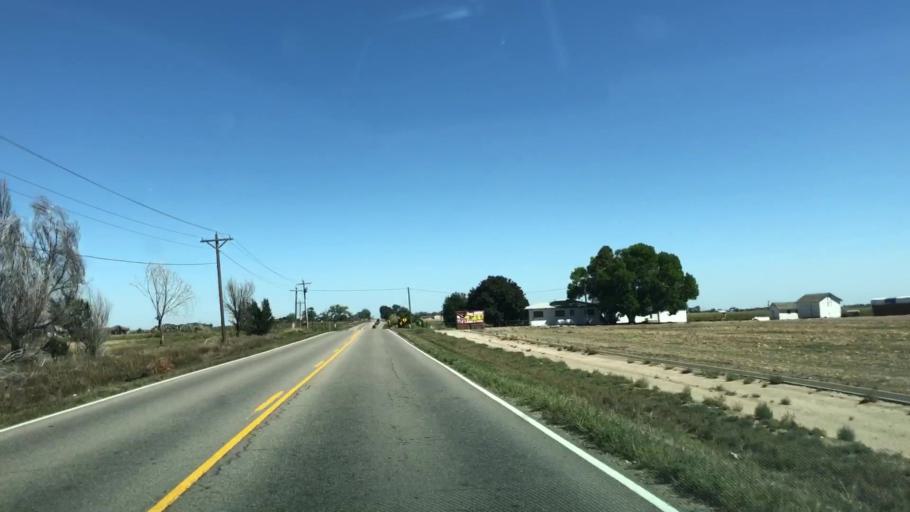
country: US
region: Colorado
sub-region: Weld County
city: Windsor
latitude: 40.5228
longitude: -104.9322
